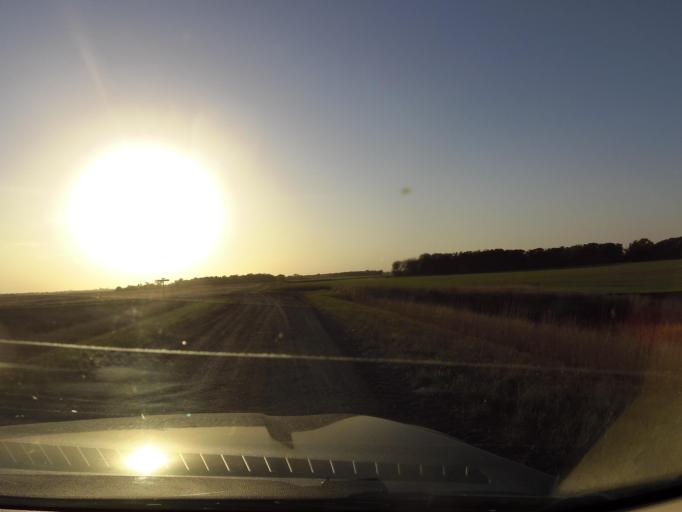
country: US
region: North Dakota
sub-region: Walsh County
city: Grafton
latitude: 48.4199
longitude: -97.4694
